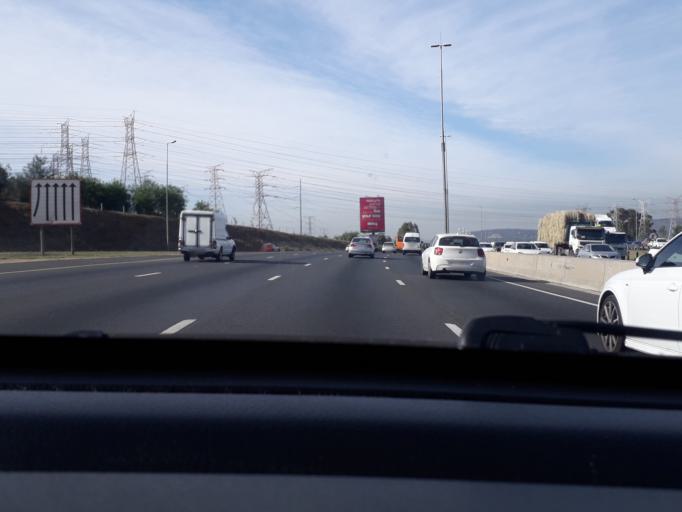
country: ZA
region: Gauteng
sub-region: City of Johannesburg Metropolitan Municipality
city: Modderfontein
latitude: -26.1244
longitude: 28.1363
